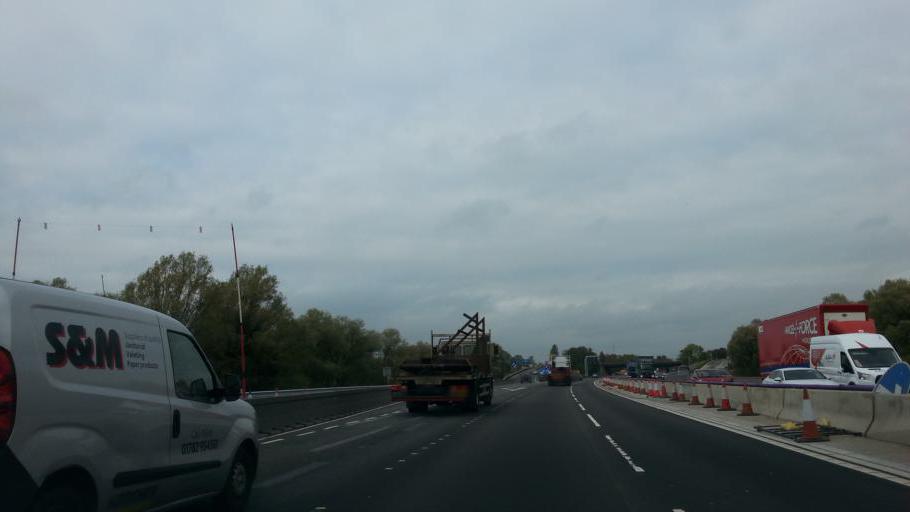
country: GB
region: England
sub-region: Cheshire East
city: Holmes Chapel
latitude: 53.1960
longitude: -2.3857
